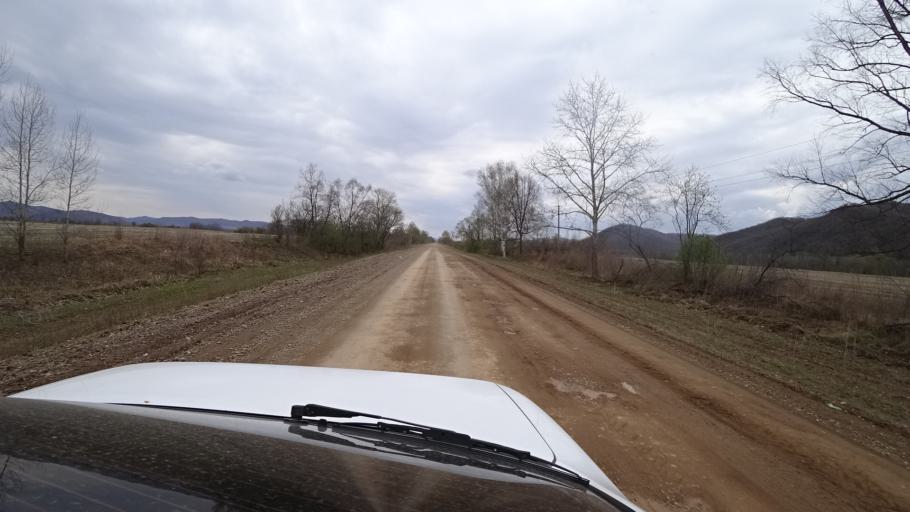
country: RU
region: Primorskiy
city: Novopokrovka
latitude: 45.5662
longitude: 134.3271
